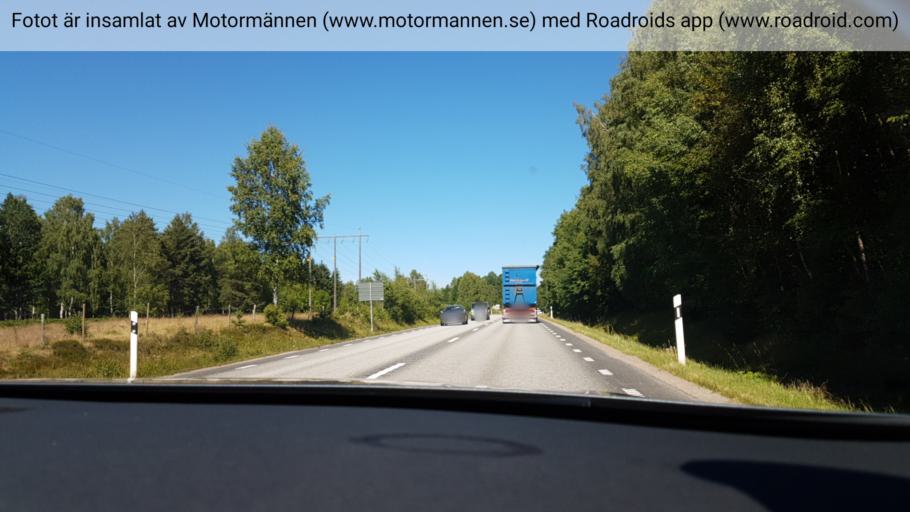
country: SE
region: Joenkoeping
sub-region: Varnamo Kommun
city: Varnamo
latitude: 57.1963
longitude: 14.0727
